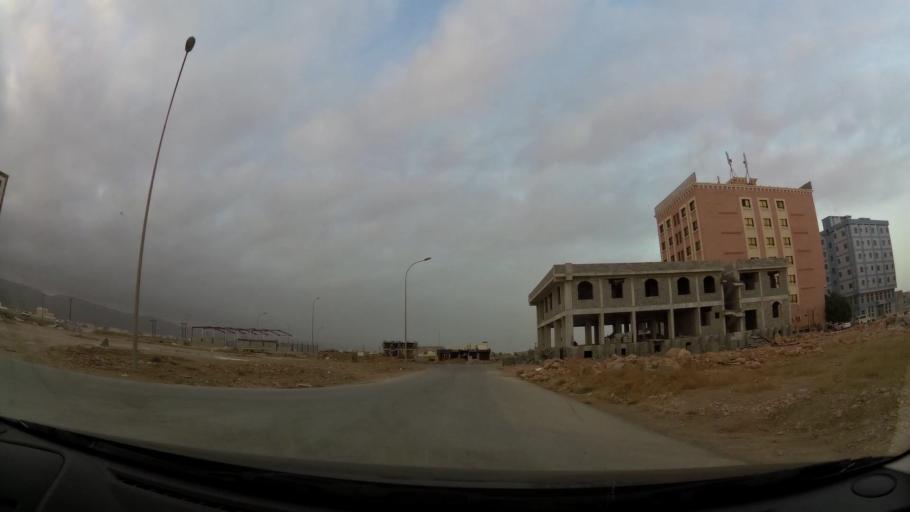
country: OM
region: Zufar
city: Salalah
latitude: 17.0283
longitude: 54.0280
